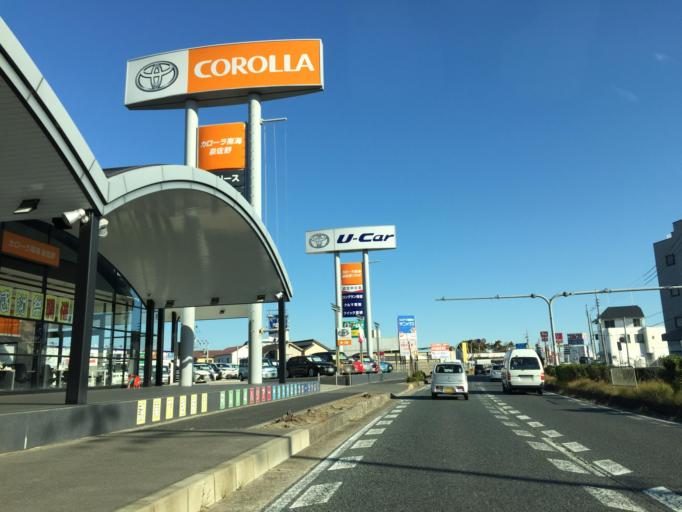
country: JP
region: Osaka
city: Kaizuka
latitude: 34.4237
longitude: 135.3401
